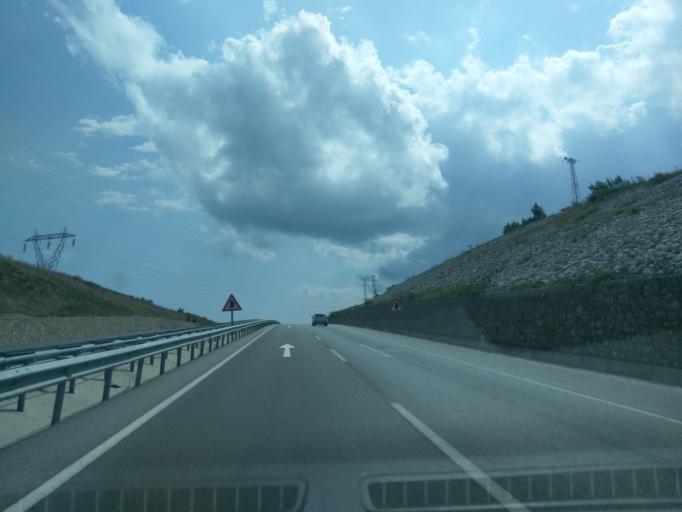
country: TR
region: Sinop
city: Kabali
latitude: 41.8538
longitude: 35.1154
